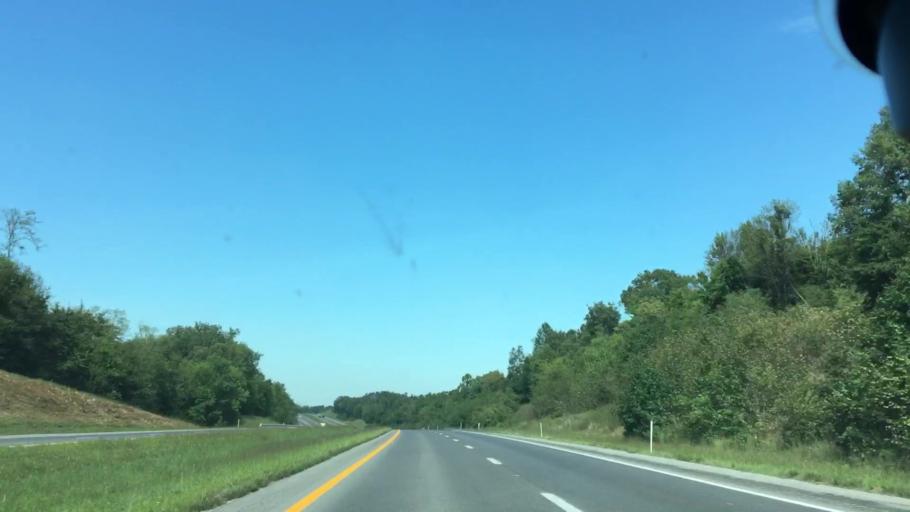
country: US
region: Kentucky
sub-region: Webster County
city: Sebree
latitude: 37.5288
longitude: -87.4759
